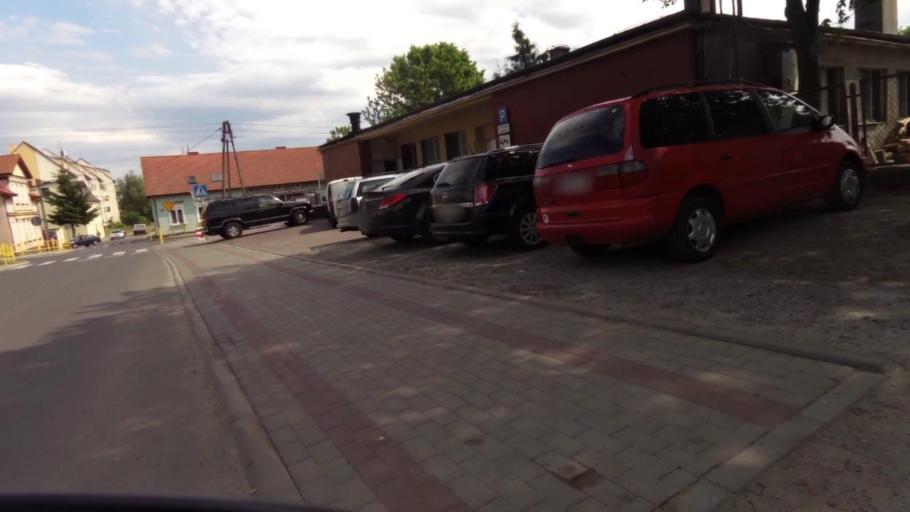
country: PL
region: West Pomeranian Voivodeship
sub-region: Powiat kamienski
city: Wolin
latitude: 53.8421
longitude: 14.6109
